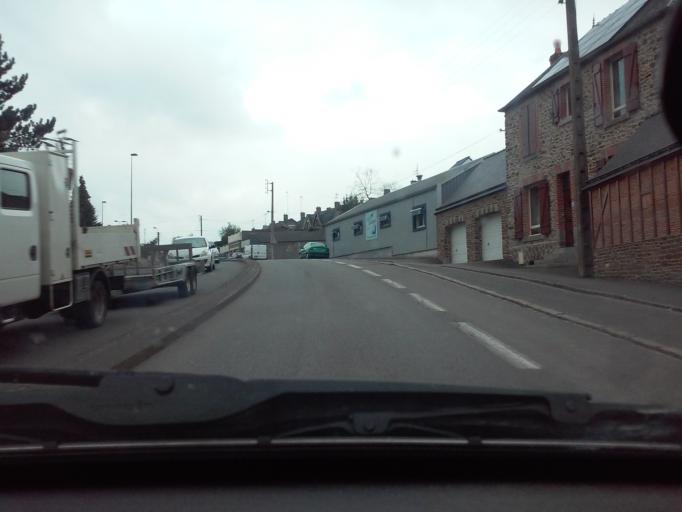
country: FR
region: Brittany
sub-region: Departement d'Ille-et-Vilaine
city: Fougeres
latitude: 48.3468
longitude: -1.1855
